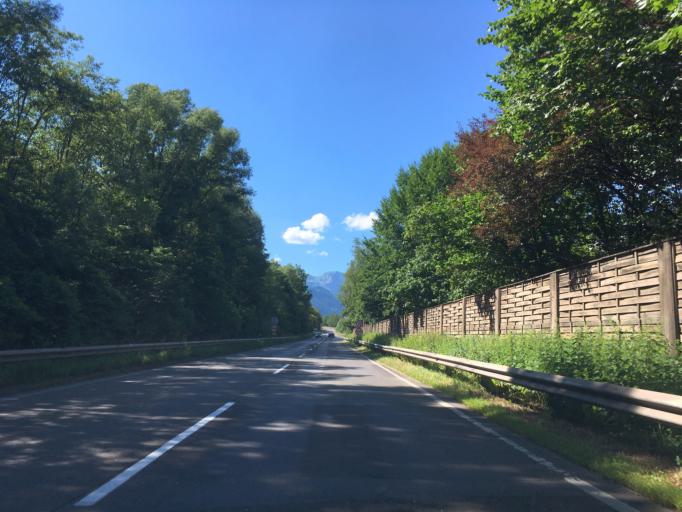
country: AT
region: Styria
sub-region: Politischer Bezirk Leoben
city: Sankt Peter-Freienstein
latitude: 47.4062
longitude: 15.0291
